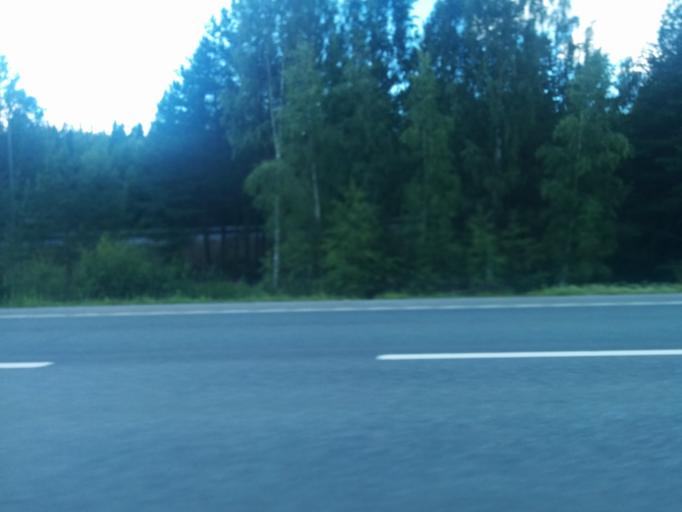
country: FI
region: Pirkanmaa
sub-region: Tampere
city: Kangasala
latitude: 61.5312
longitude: 23.9491
